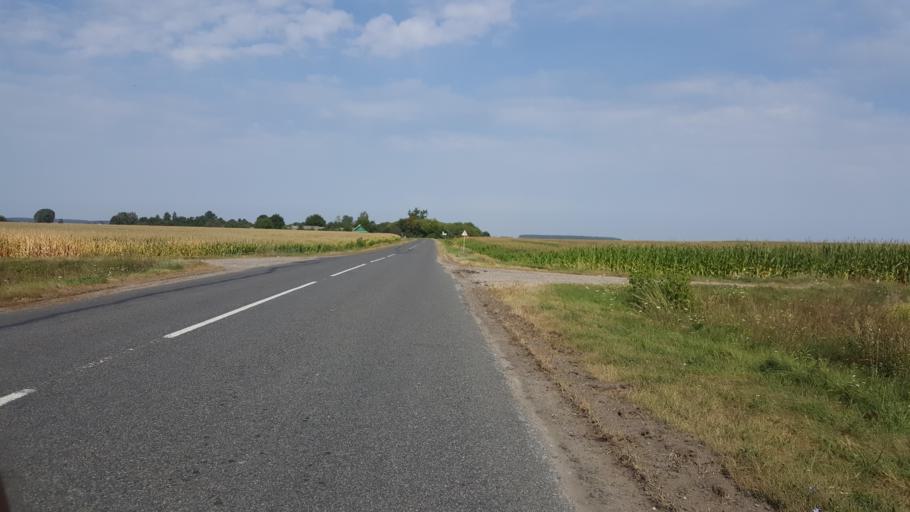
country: BY
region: Brest
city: Kamyanyets
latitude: 52.4225
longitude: 23.7738
